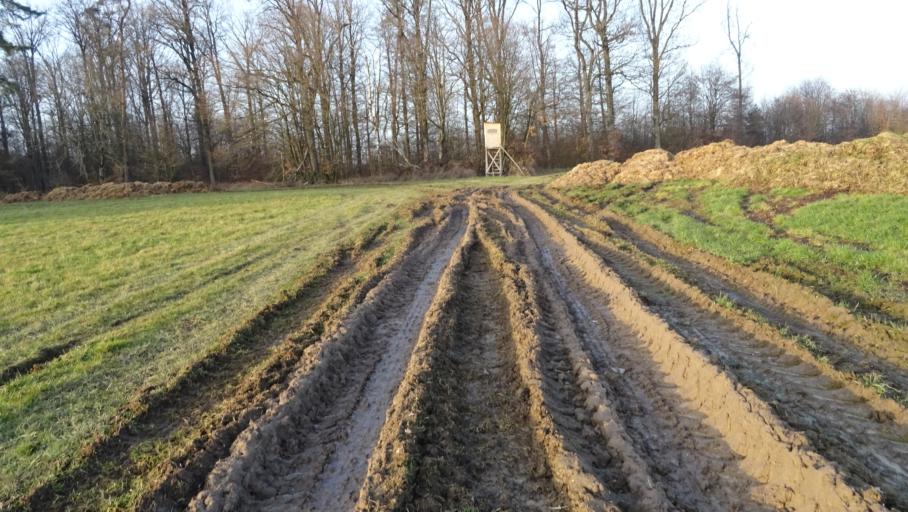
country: DE
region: Baden-Wuerttemberg
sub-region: Karlsruhe Region
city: Neckargerach
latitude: 49.4055
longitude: 9.1115
